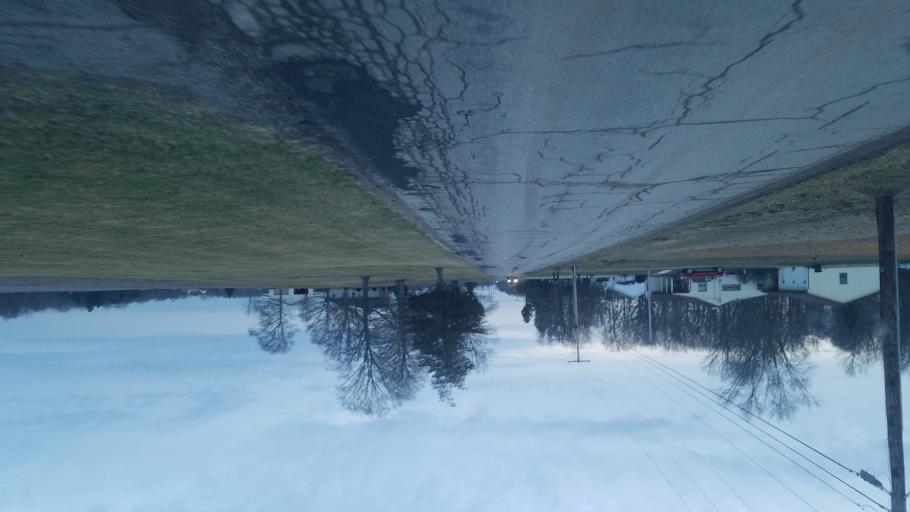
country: US
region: Ohio
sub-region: Morrow County
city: Mount Gilead
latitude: 40.5488
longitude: -82.8628
